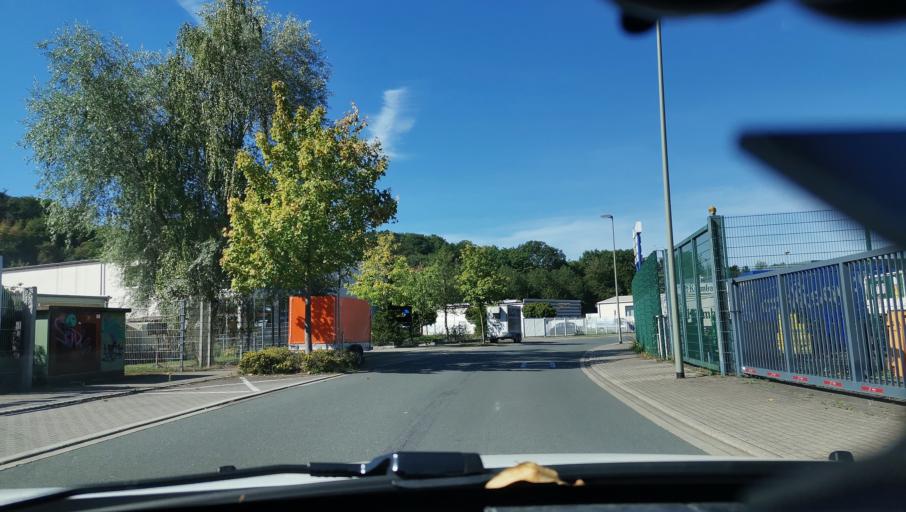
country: DE
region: North Rhine-Westphalia
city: Wetter (Ruhr)
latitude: 51.3806
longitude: 7.3861
